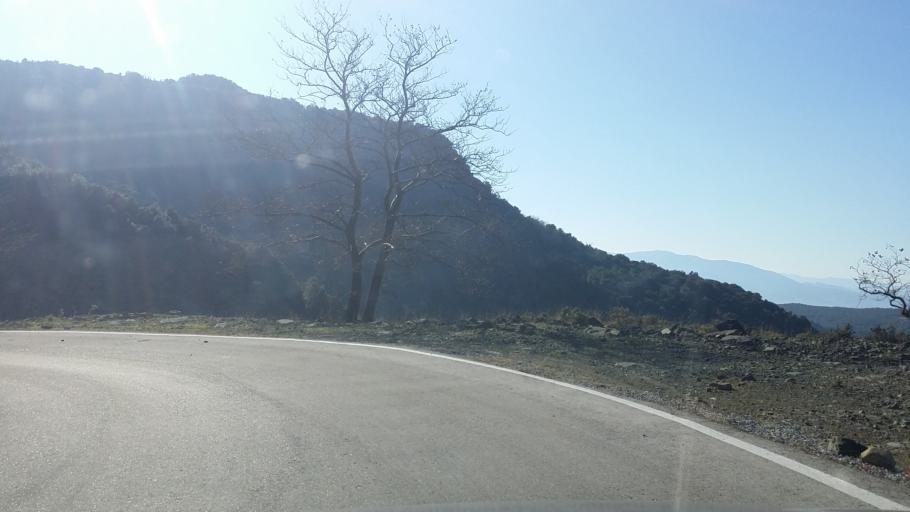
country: GR
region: West Greece
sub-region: Nomos Aitolias kai Akarnanias
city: Krikellos
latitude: 38.9722
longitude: 21.2747
